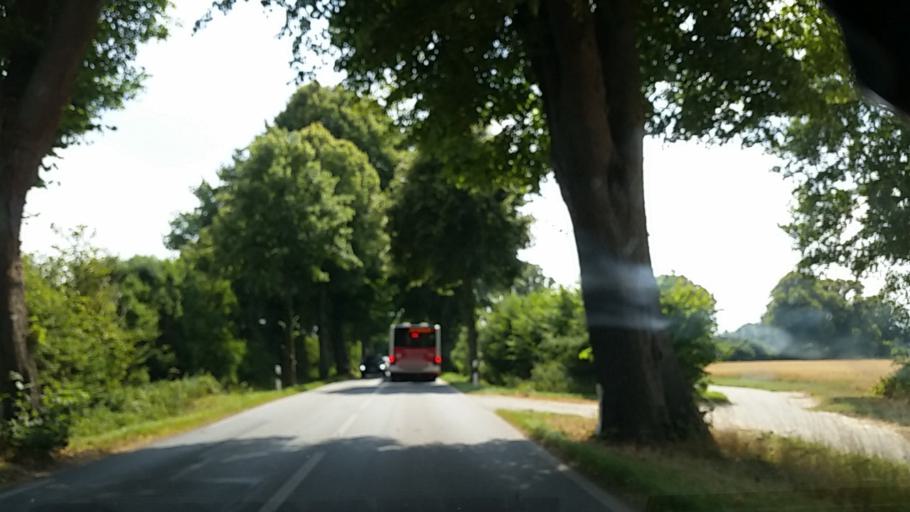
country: DE
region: Schleswig-Holstein
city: Schmilau
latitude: 53.6659
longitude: 10.7674
